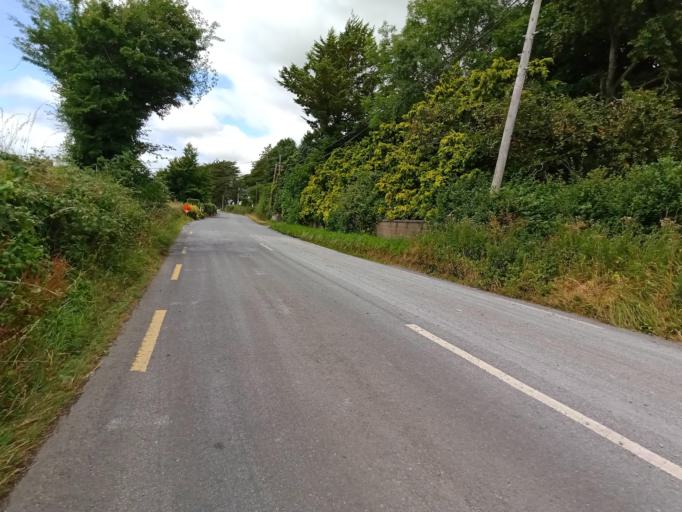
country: IE
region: Leinster
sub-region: Kilkenny
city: Callan
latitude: 52.5527
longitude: -7.4024
